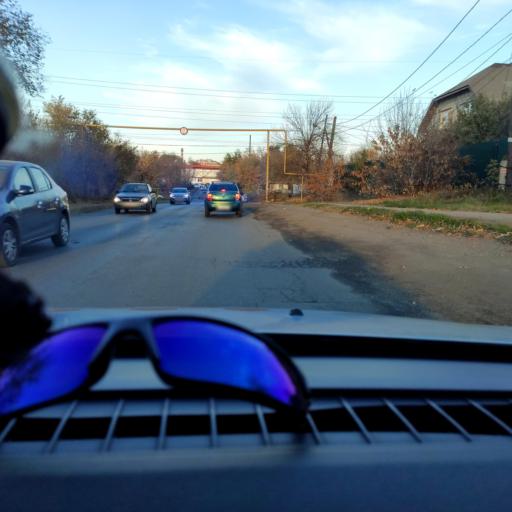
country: RU
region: Samara
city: Samara
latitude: 53.1846
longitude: 50.1572
